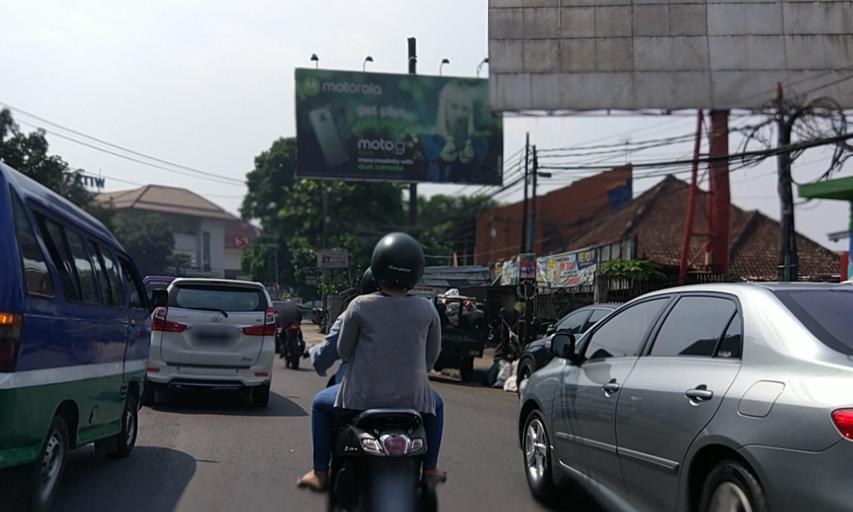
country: ID
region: West Java
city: Bandung
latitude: -6.9043
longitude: 107.6048
